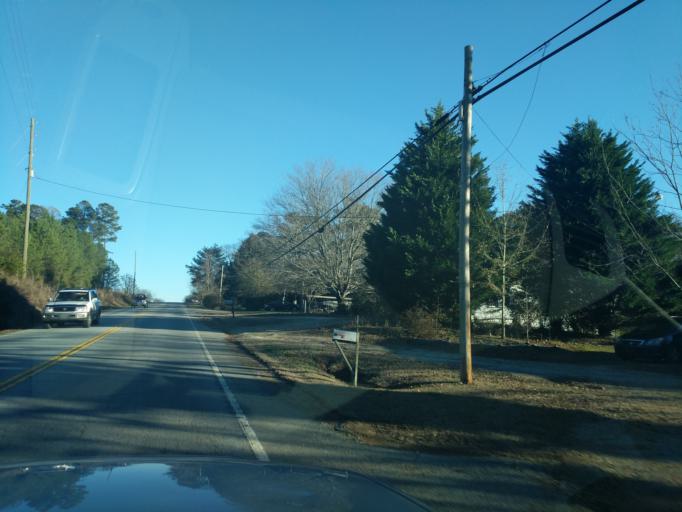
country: US
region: South Carolina
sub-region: Oconee County
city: Westminster
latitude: 34.6827
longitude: -83.1261
